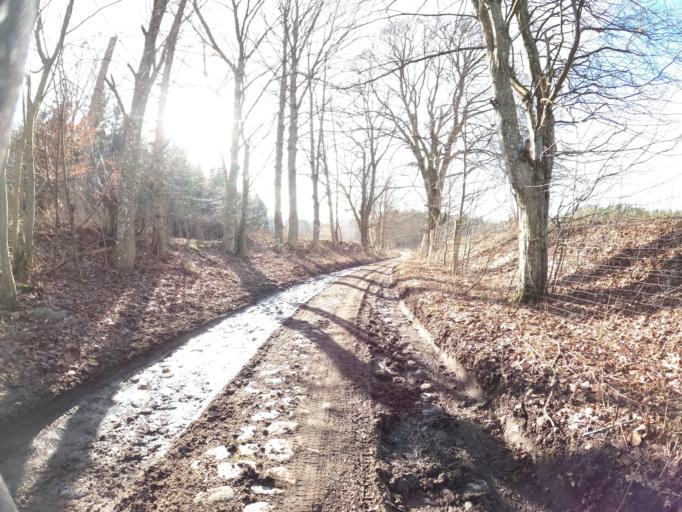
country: PL
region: West Pomeranian Voivodeship
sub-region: Powiat koszalinski
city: Polanow
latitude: 54.2342
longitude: 16.6420
